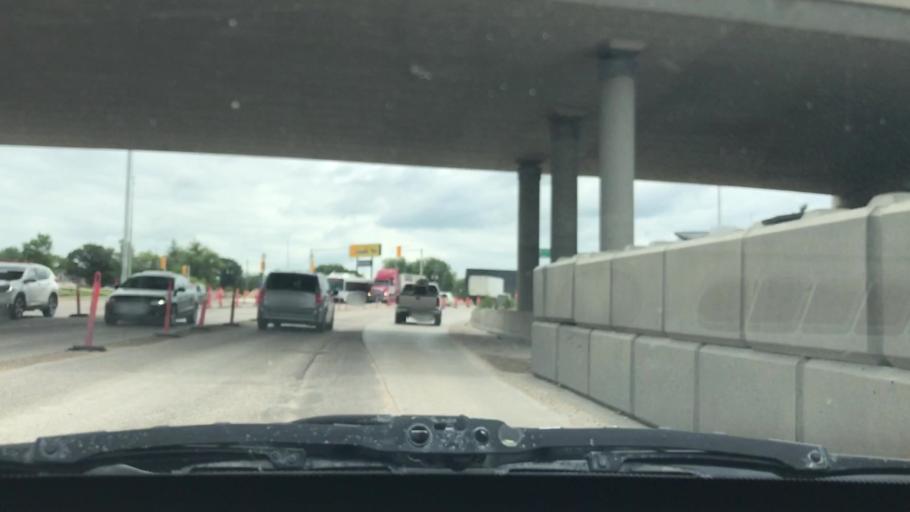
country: CA
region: Manitoba
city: Winnipeg
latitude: 49.8538
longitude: -97.1524
